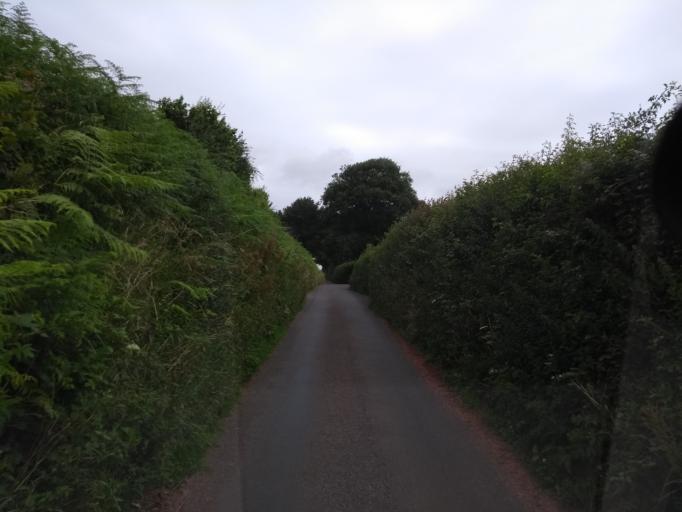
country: GB
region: England
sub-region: Somerset
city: Bishops Lydeard
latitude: 51.0403
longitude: -3.2372
